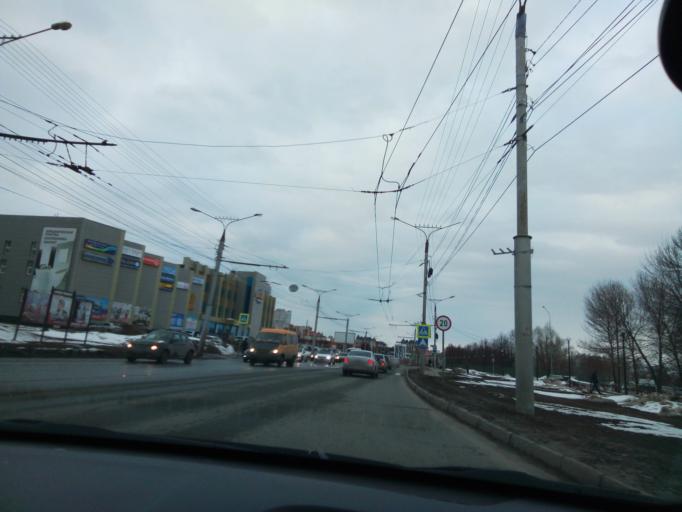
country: RU
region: Chuvashia
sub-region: Cheboksarskiy Rayon
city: Cheboksary
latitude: 56.1444
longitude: 47.2053
